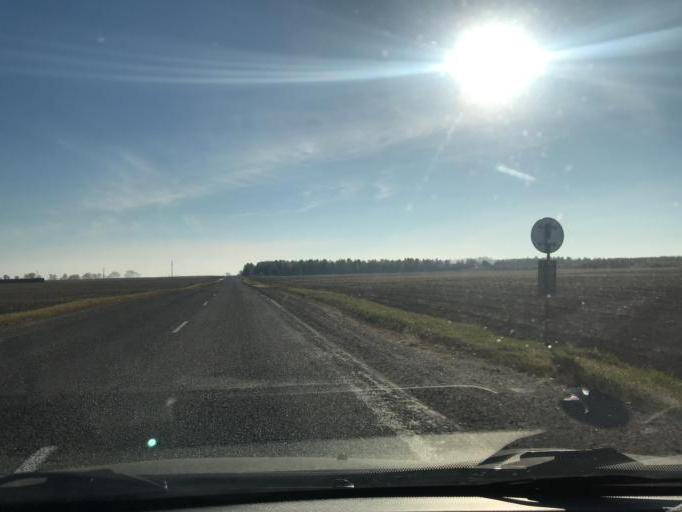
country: BY
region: Gomel
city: Brahin
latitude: 51.7860
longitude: 30.2012
